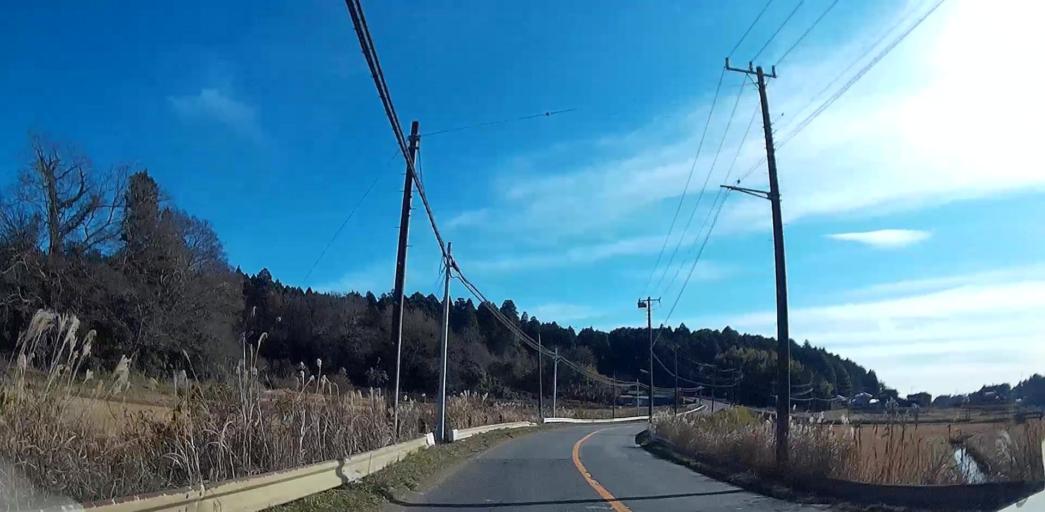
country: JP
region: Chiba
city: Yokaichiba
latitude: 35.7616
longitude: 140.4499
